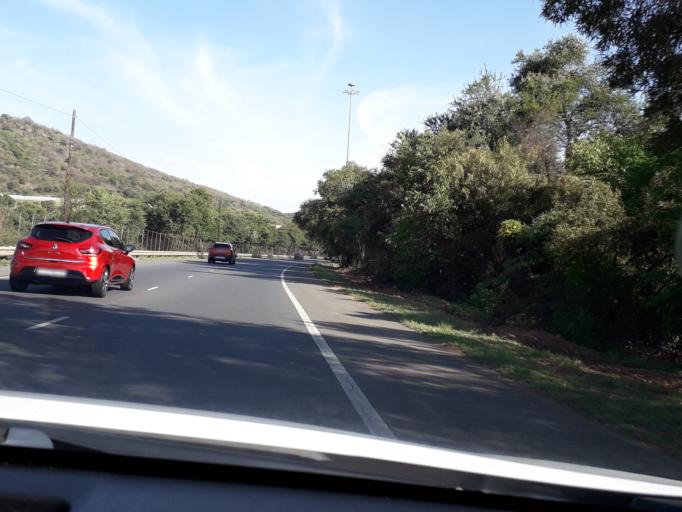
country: ZA
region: Gauteng
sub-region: City of Tshwane Metropolitan Municipality
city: Pretoria
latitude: -25.7700
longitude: 28.1967
